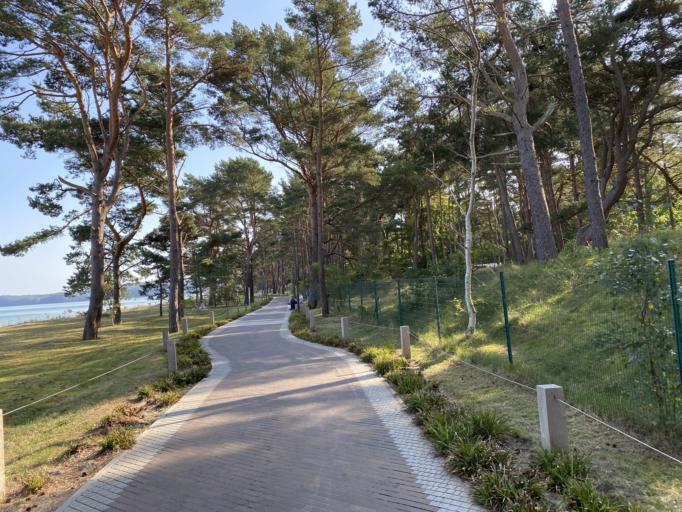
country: DE
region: Mecklenburg-Vorpommern
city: Ostseebad Binz
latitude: 54.4212
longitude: 13.5904
